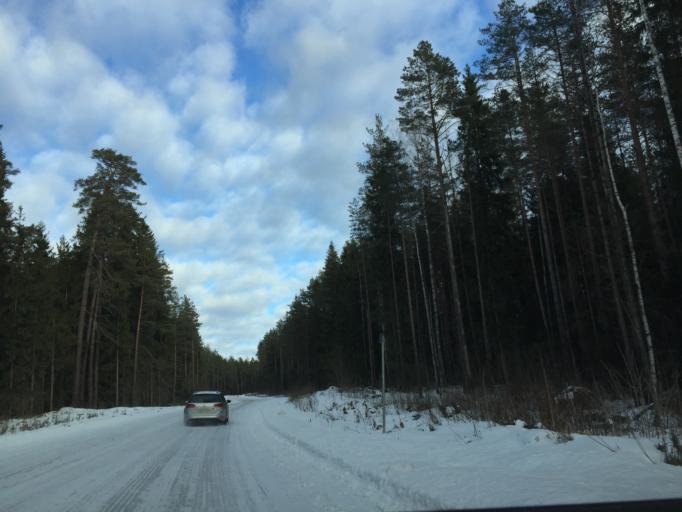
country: LV
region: Ogre
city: Jumprava
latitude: 56.5562
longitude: 24.9009
